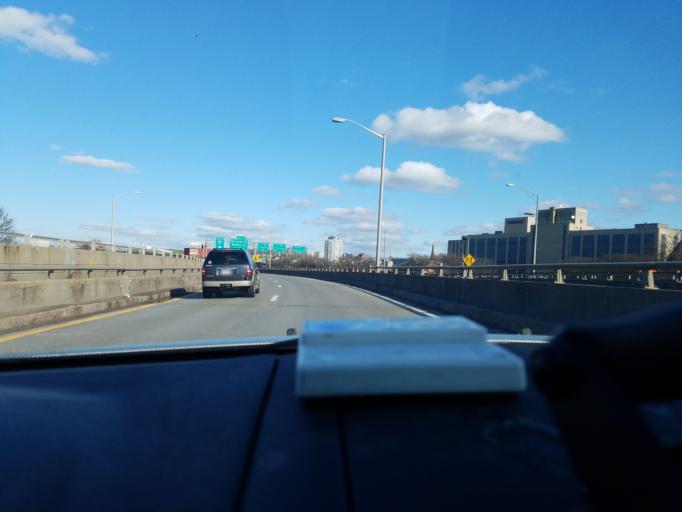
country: US
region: New York
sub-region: Onondaga County
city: Syracuse
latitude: 43.0420
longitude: -76.1482
